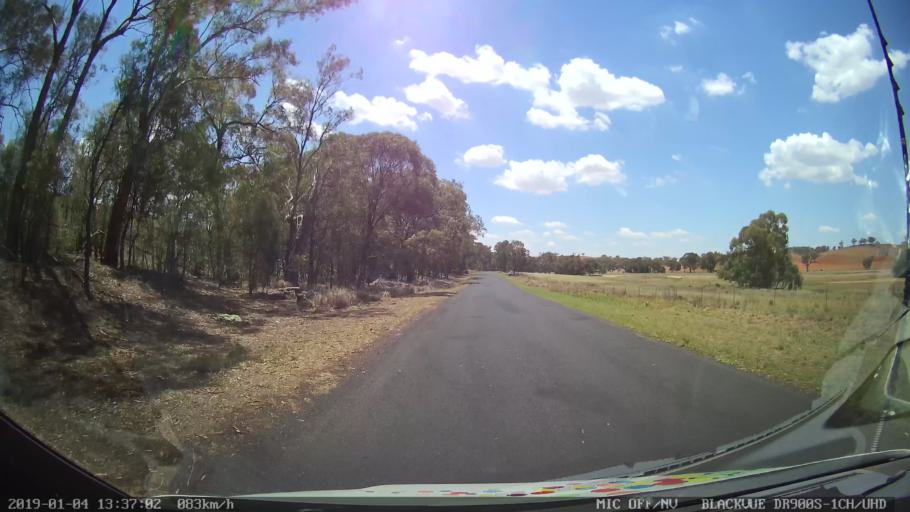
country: AU
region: New South Wales
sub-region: Dubbo Municipality
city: Dubbo
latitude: -32.5540
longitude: 148.5395
